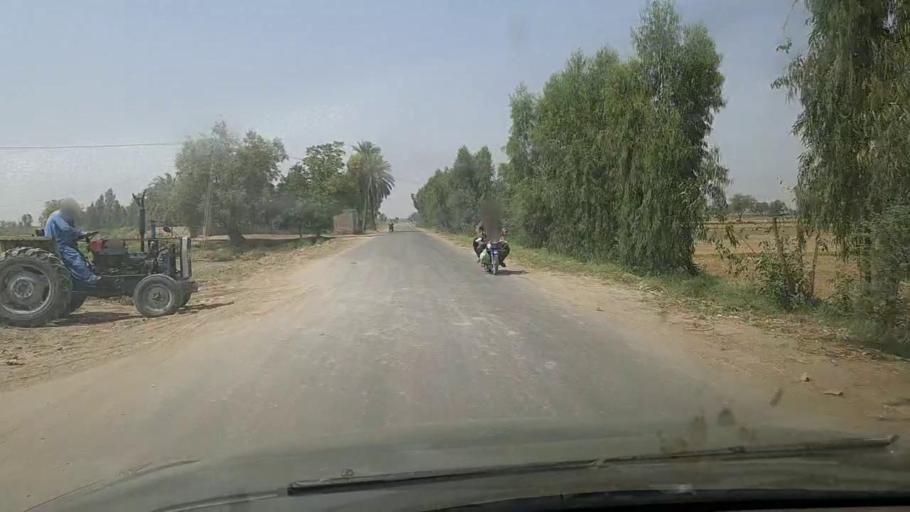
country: PK
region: Sindh
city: Khanpur
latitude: 27.8664
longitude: 69.4445
